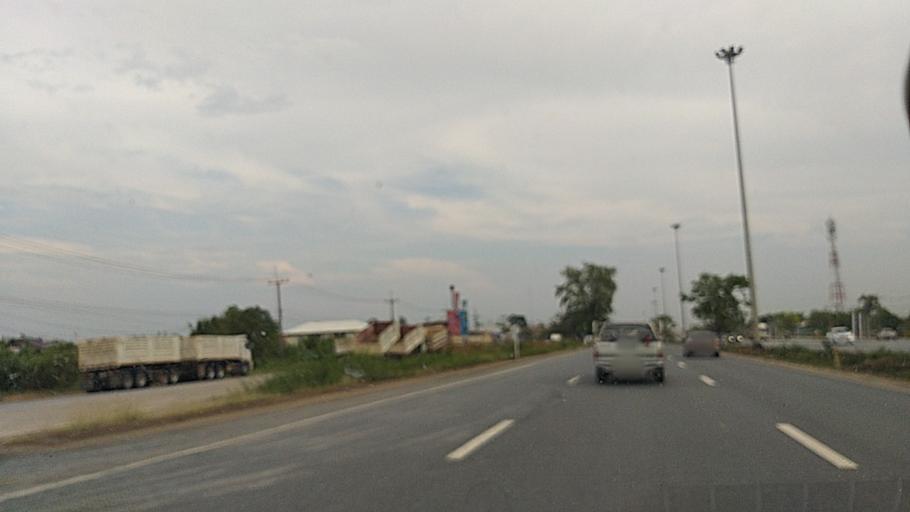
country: TH
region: Phra Nakhon Si Ayutthaya
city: Bang Pa-in
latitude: 14.2001
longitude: 100.5503
